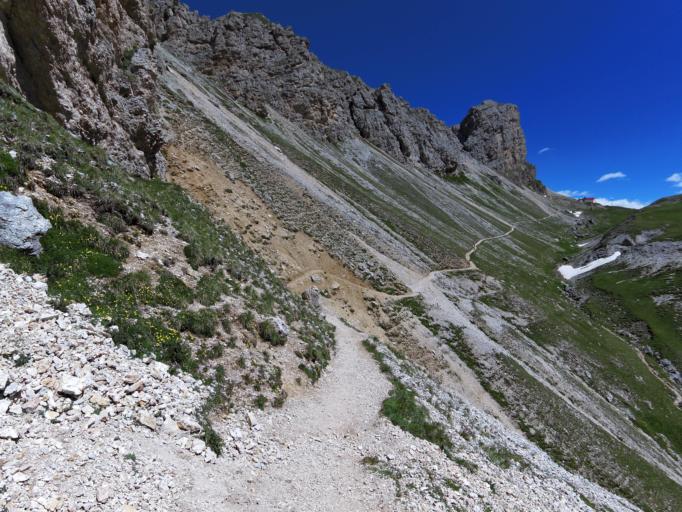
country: IT
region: Trentino-Alto Adige
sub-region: Bolzano
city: Siusi
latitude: 46.4970
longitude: 11.6219
